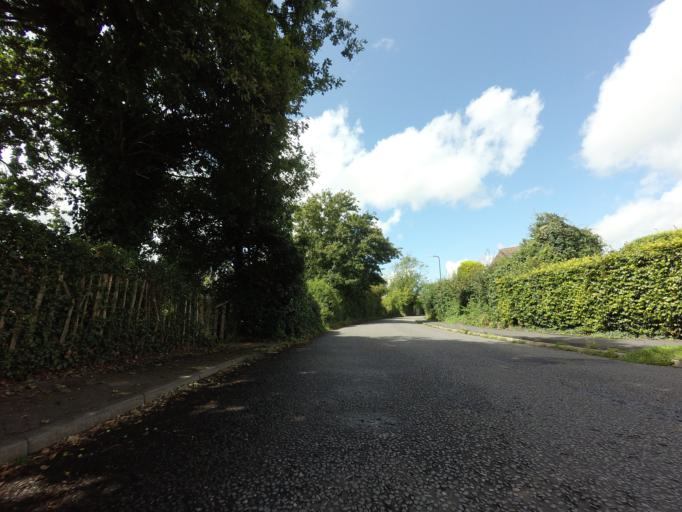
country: GB
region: England
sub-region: Kent
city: Hadlow
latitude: 51.2240
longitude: 0.3350
